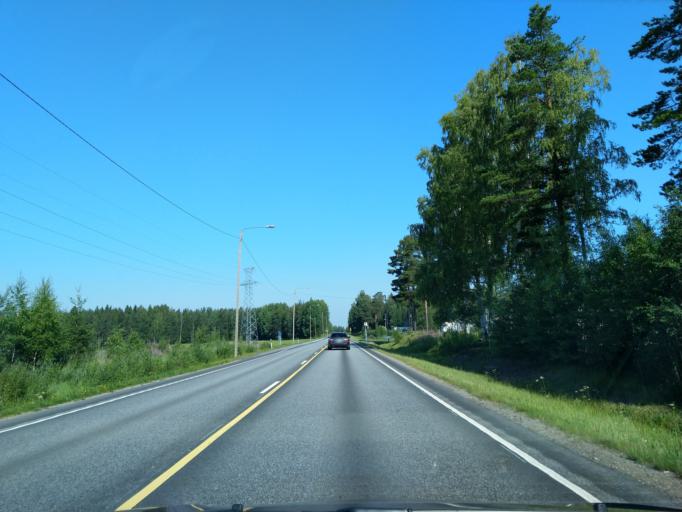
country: FI
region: Satakunta
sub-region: Pori
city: Huittinen
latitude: 61.1557
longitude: 22.7293
